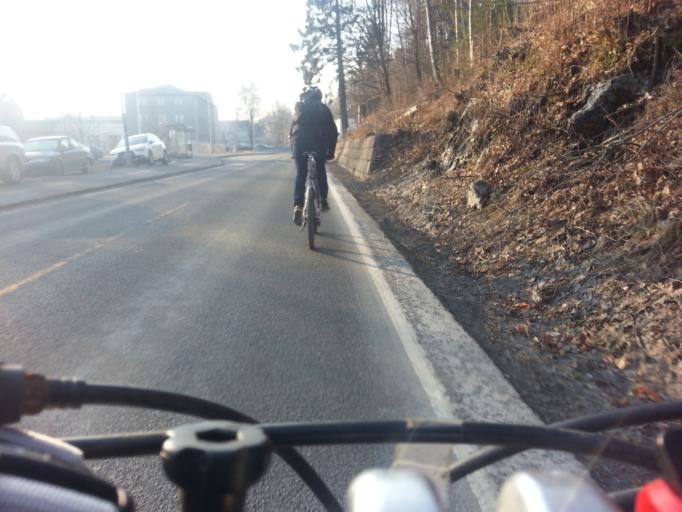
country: NO
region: Sor-Trondelag
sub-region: Trondheim
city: Trondheim
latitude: 63.4206
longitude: 10.3767
